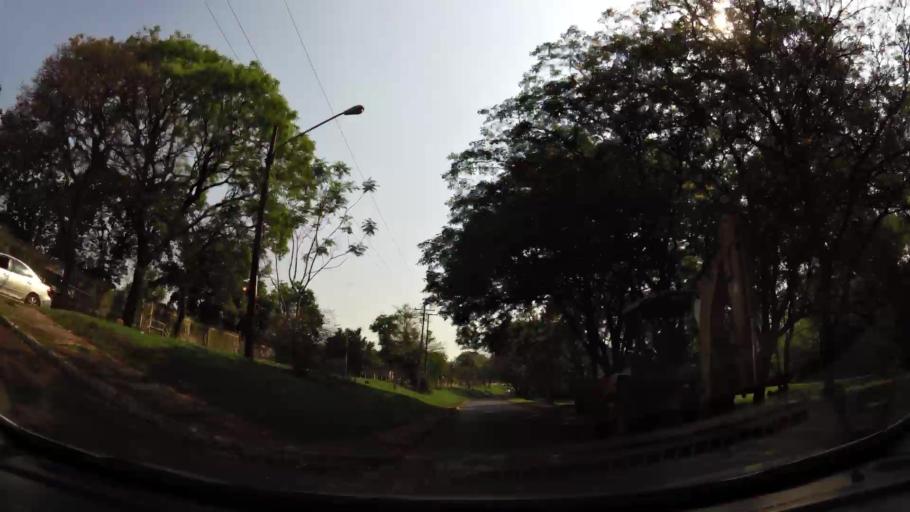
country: PY
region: Alto Parana
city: Ciudad del Este
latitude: -25.5154
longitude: -54.6386
